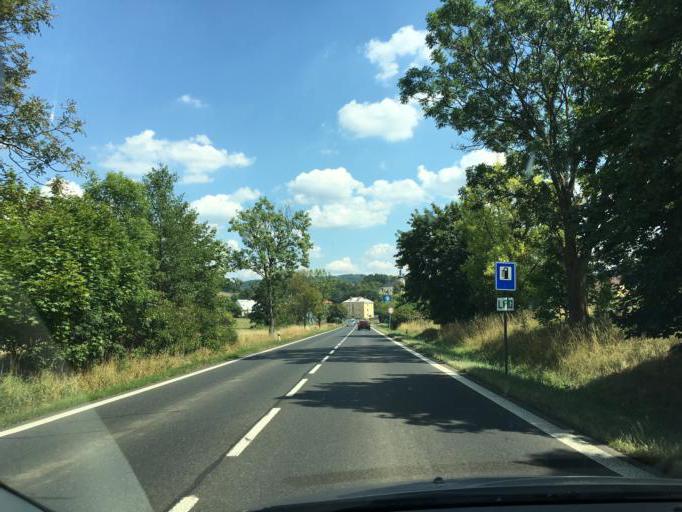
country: CZ
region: Ustecky
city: Ceska Kamenice
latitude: 50.7847
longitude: 14.3585
